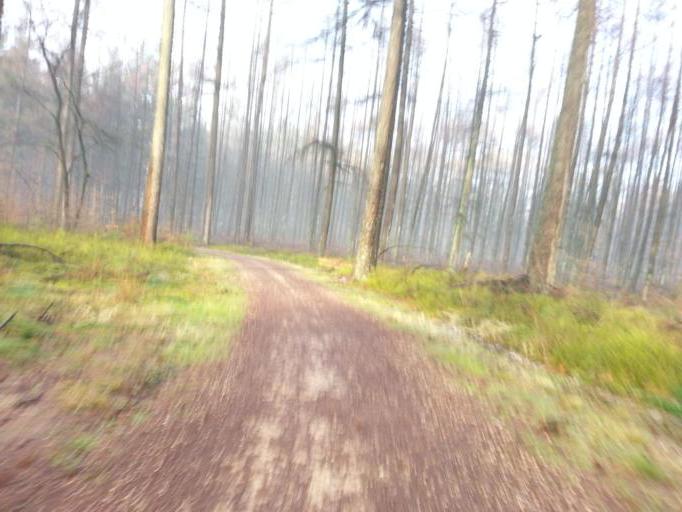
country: NL
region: Utrecht
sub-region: Gemeente Utrechtse Heuvelrug
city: Maarsbergen
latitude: 52.0342
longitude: 5.3982
